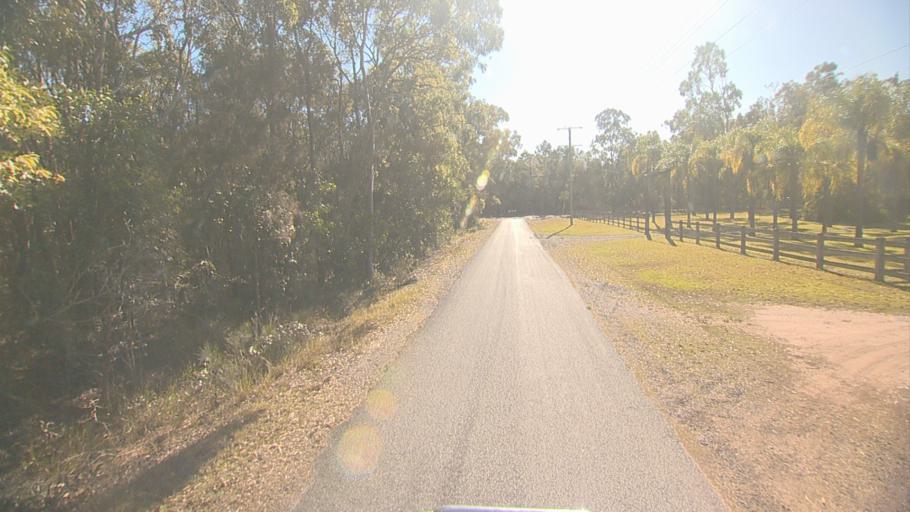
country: AU
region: Queensland
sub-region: Logan
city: Park Ridge South
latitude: -27.7480
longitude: 153.0485
